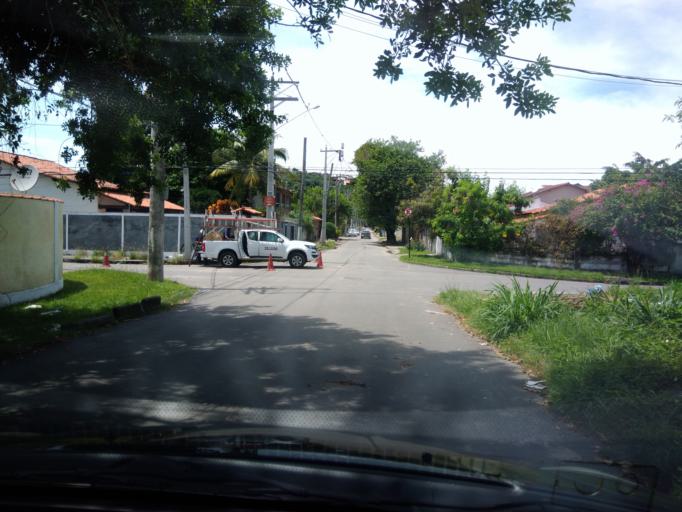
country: BR
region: Rio de Janeiro
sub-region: Niteroi
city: Niteroi
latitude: -22.9380
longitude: -43.0650
